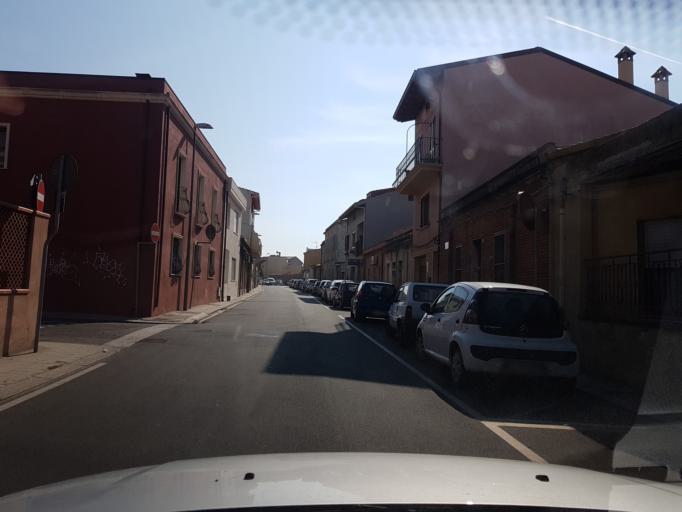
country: IT
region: Sardinia
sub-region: Provincia di Oristano
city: Oristano
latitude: 39.8998
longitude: 8.5956
